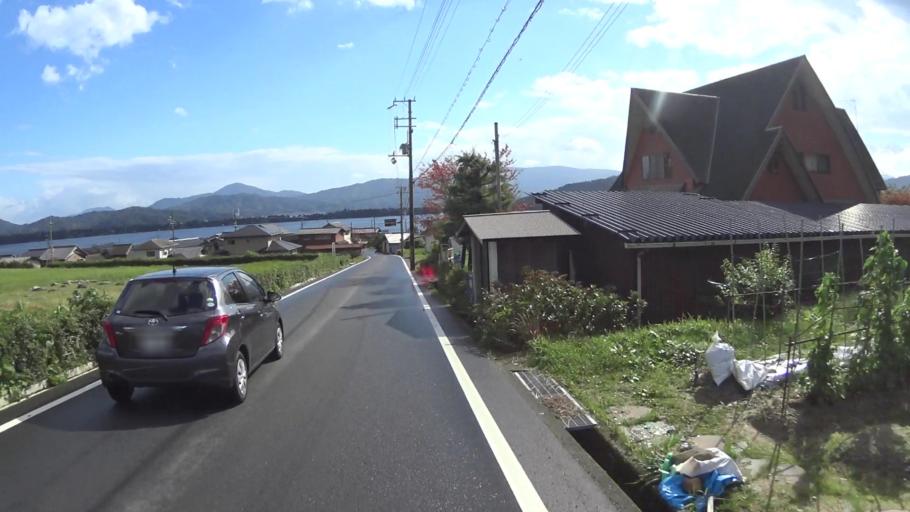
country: JP
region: Kyoto
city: Miyazu
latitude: 35.5791
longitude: 135.1787
